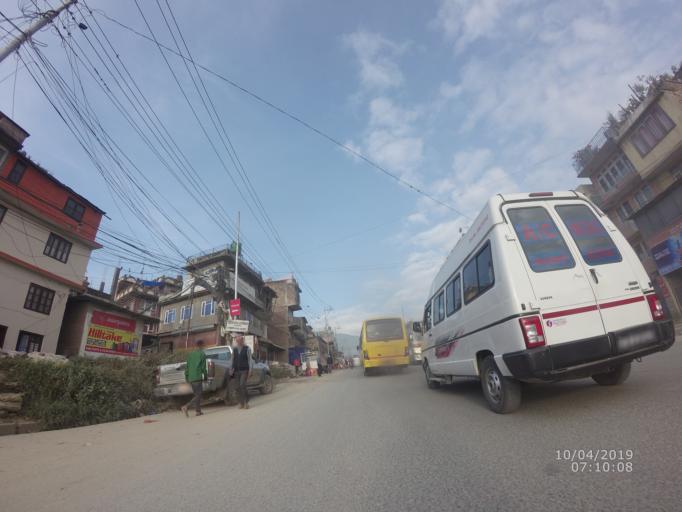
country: NP
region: Central Region
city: Kirtipur
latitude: 27.6876
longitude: 85.2430
